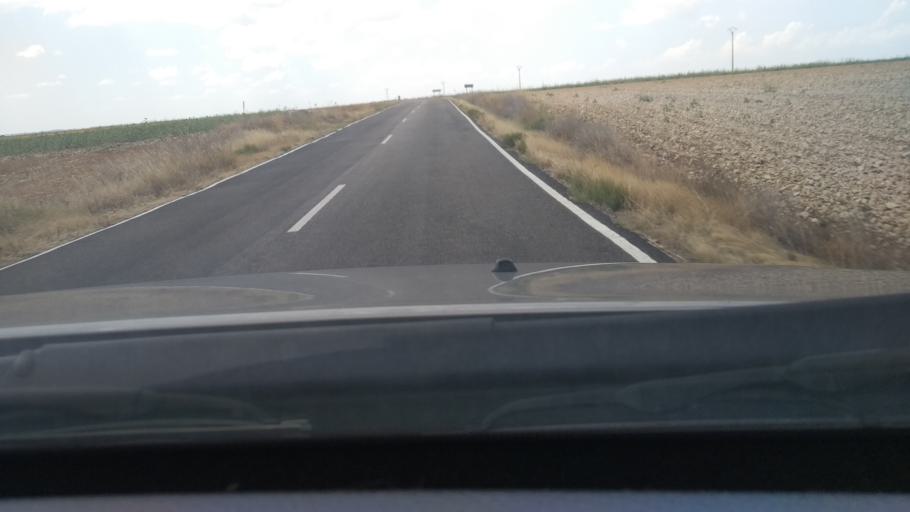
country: ES
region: Castille and Leon
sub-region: Provincia de Burgos
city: Iglesiarrubia
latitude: 41.9433
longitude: -3.8621
